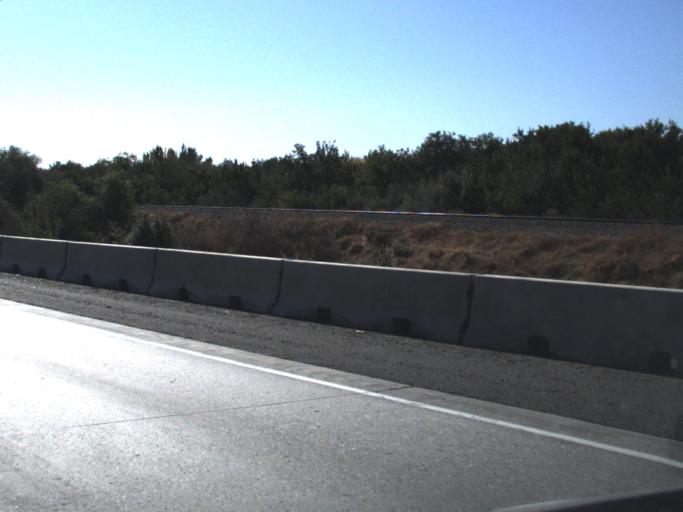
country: US
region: Washington
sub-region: Benton County
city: Richland
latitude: 46.2518
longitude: -119.2562
